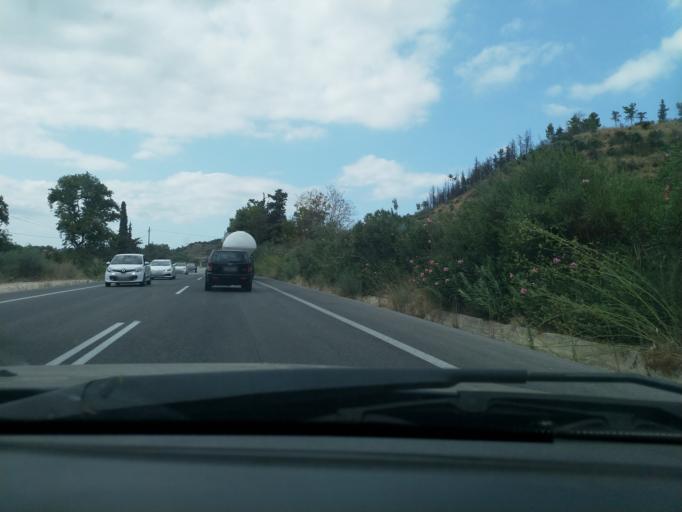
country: GR
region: Crete
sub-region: Nomos Chanias
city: Georgioupolis
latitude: 35.3739
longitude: 24.2103
